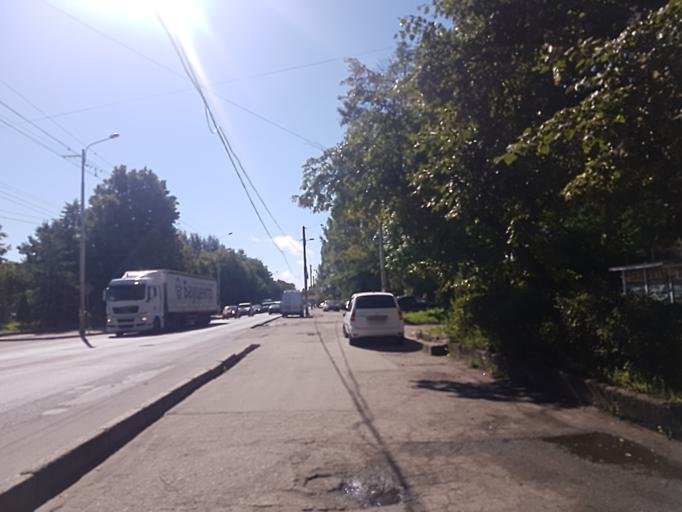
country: RU
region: Kaliningrad
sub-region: Gorod Kaliningrad
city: Kaliningrad
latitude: 54.6932
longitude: 20.5261
